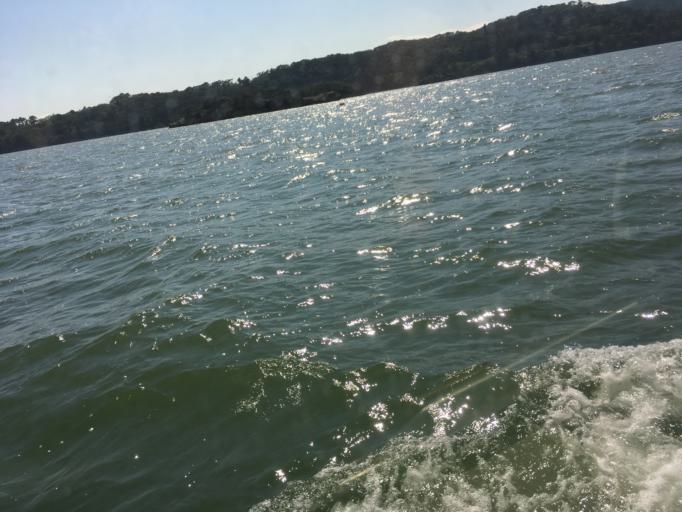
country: JP
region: Miyagi
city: Matsushima
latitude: 38.3563
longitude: 141.0735
